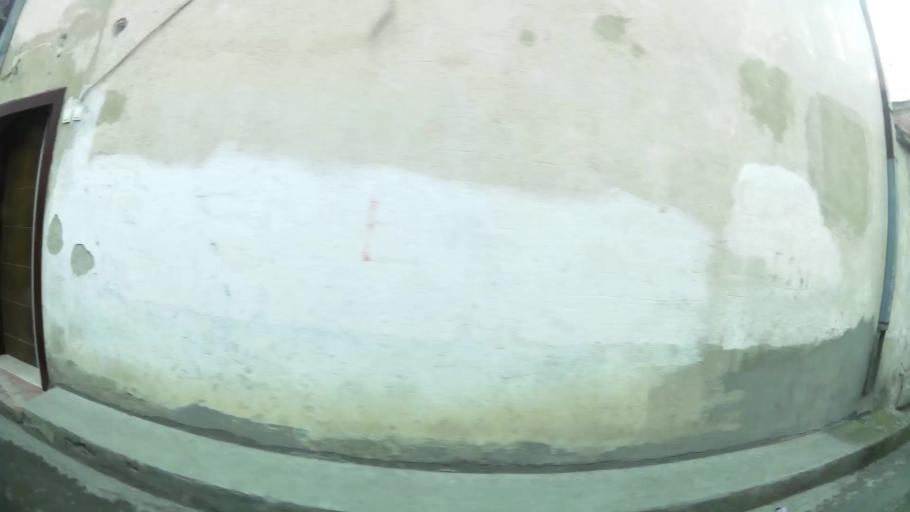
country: MK
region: Cair
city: Cair
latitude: 42.0077
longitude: 21.4398
